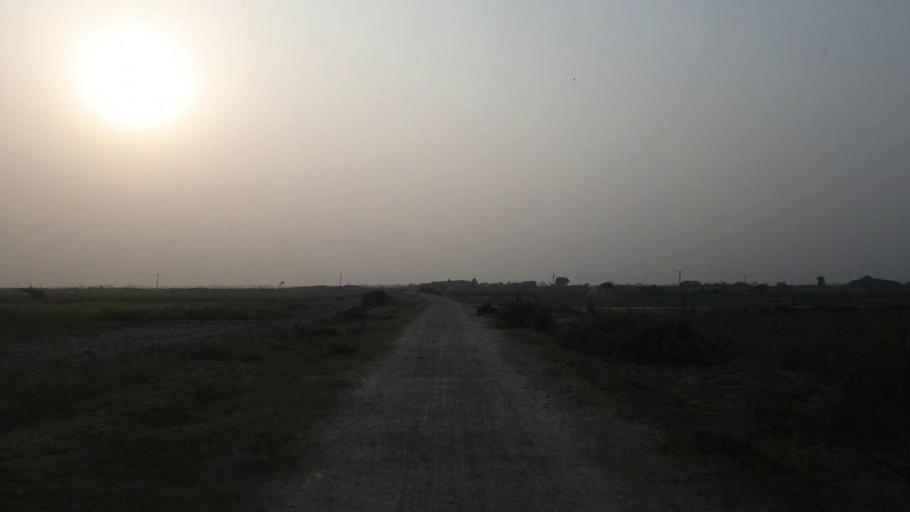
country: PK
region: Sindh
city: Mirpur Batoro
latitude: 24.6635
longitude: 68.3793
